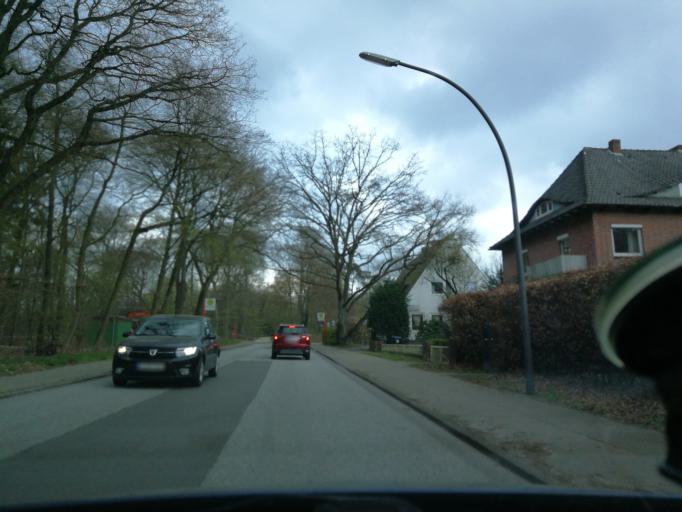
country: DE
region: Hamburg
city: Harburg
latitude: 53.4594
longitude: 9.9350
